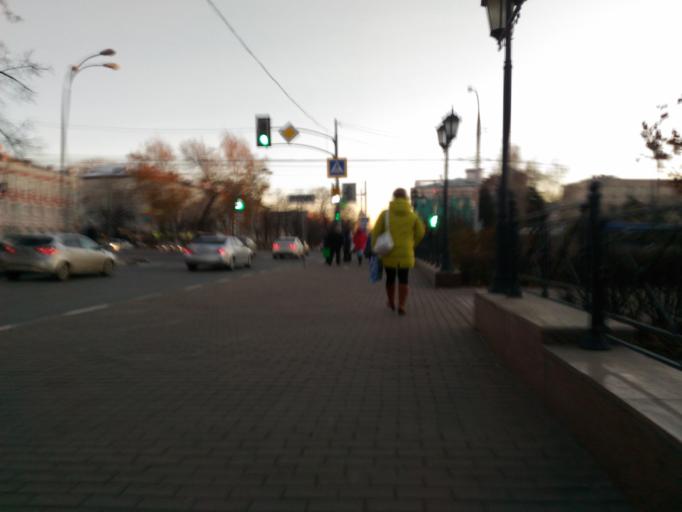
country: RU
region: Ulyanovsk
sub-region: Ulyanovskiy Rayon
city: Ulyanovsk
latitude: 54.3150
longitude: 48.3953
